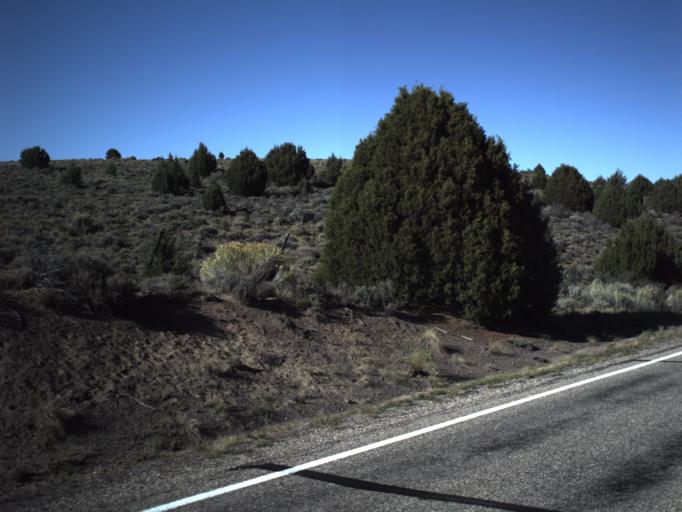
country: US
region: Utah
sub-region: Garfield County
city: Panguitch
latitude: 37.7642
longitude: -112.5544
